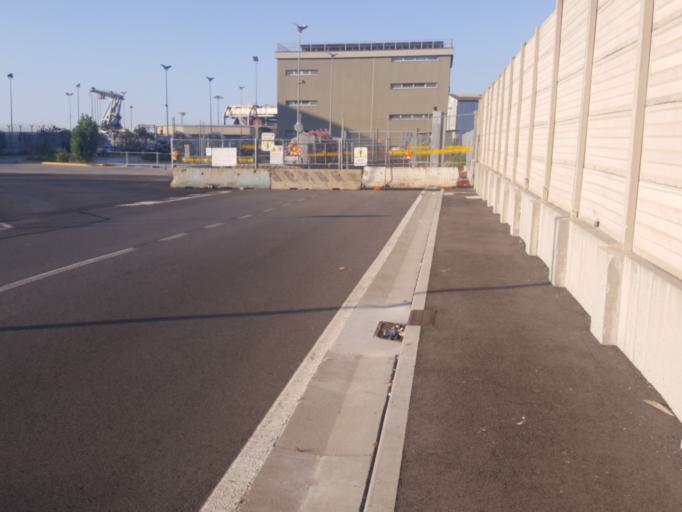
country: IT
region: Liguria
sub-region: Provincia di Genova
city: San Teodoro
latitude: 44.4099
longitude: 8.8712
